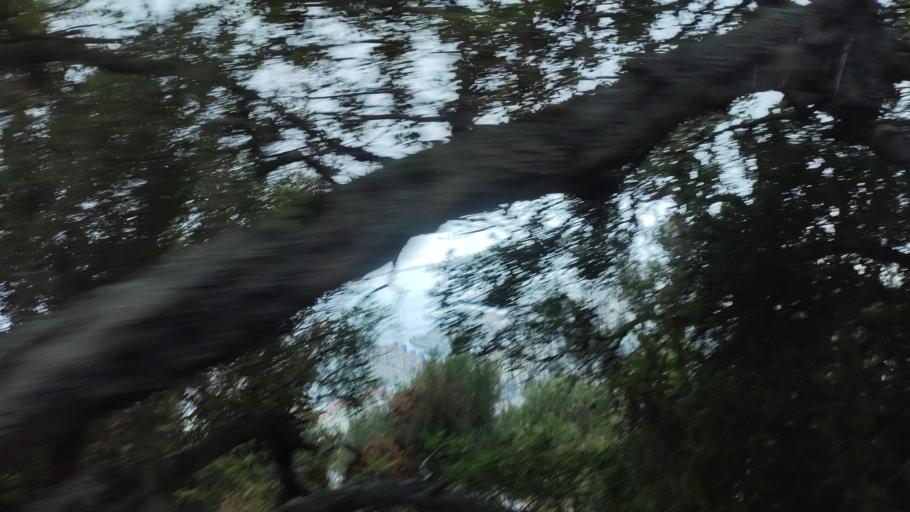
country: GI
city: Gibraltar
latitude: 36.1352
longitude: -5.3494
